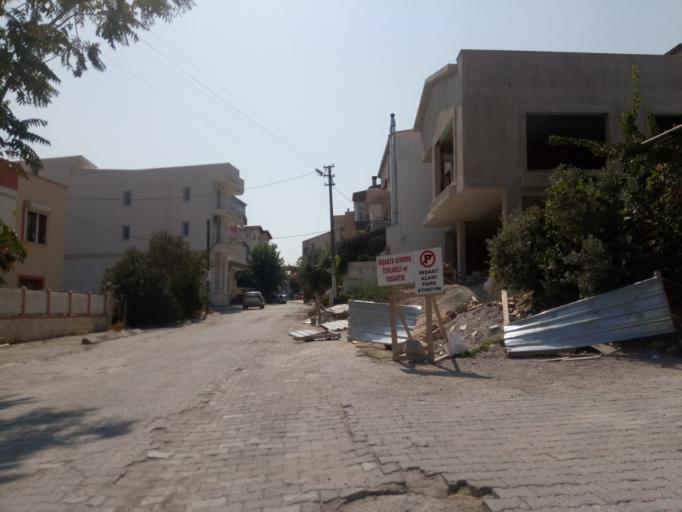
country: TR
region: Izmir
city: Urla
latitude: 38.3274
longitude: 26.7657
